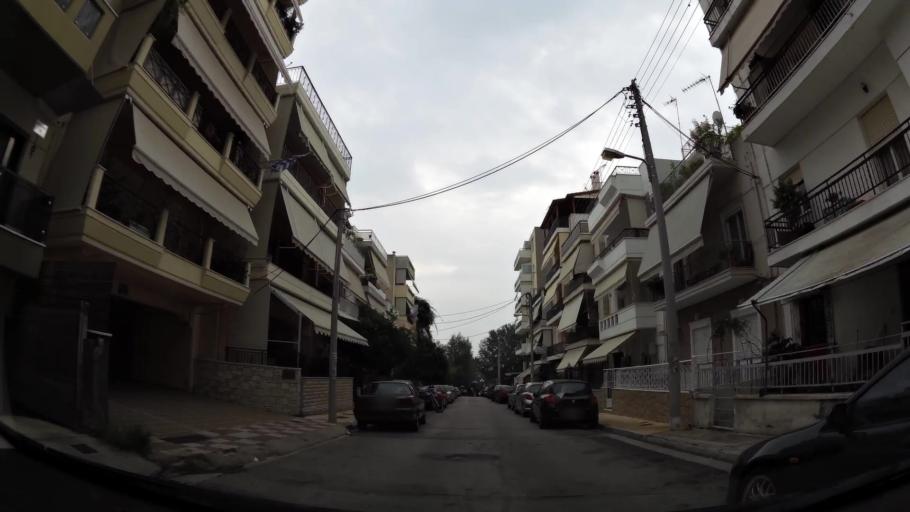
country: GR
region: Attica
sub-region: Nomos Piraios
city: Korydallos
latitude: 37.9795
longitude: 23.6343
